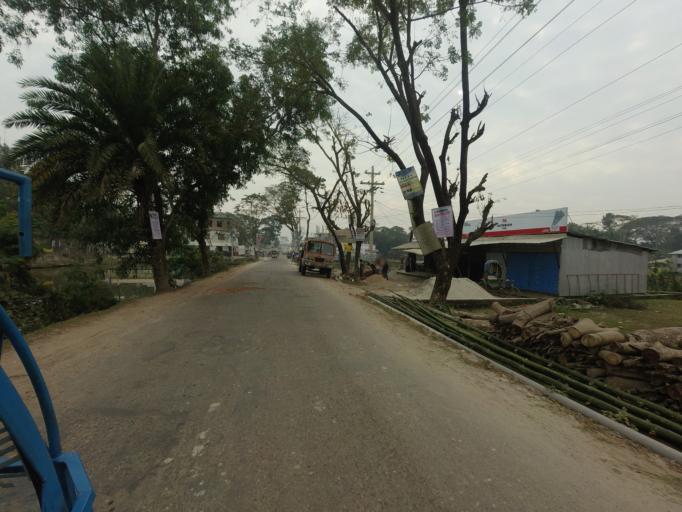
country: BD
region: Barisal
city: Nalchiti
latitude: 22.4649
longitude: 90.3775
